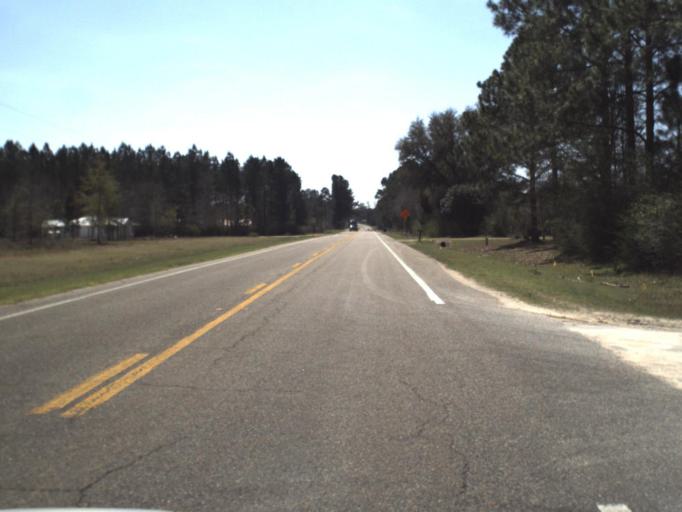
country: US
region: Florida
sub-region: Calhoun County
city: Blountstown
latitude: 30.5043
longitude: -85.0381
